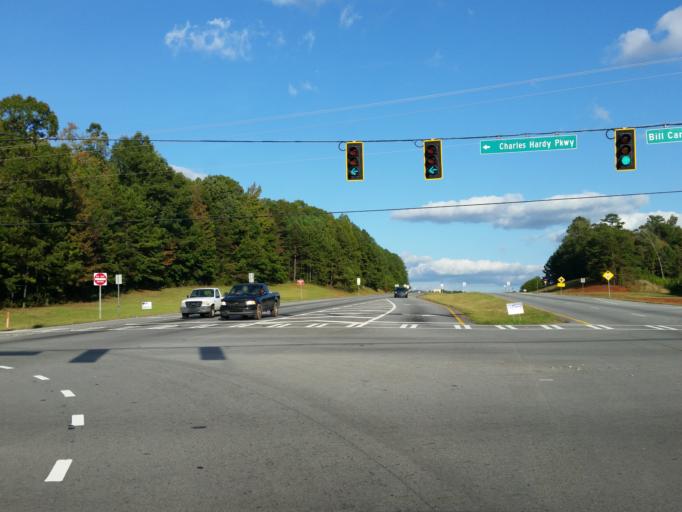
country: US
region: Georgia
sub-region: Paulding County
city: Hiram
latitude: 33.9025
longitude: -84.7791
